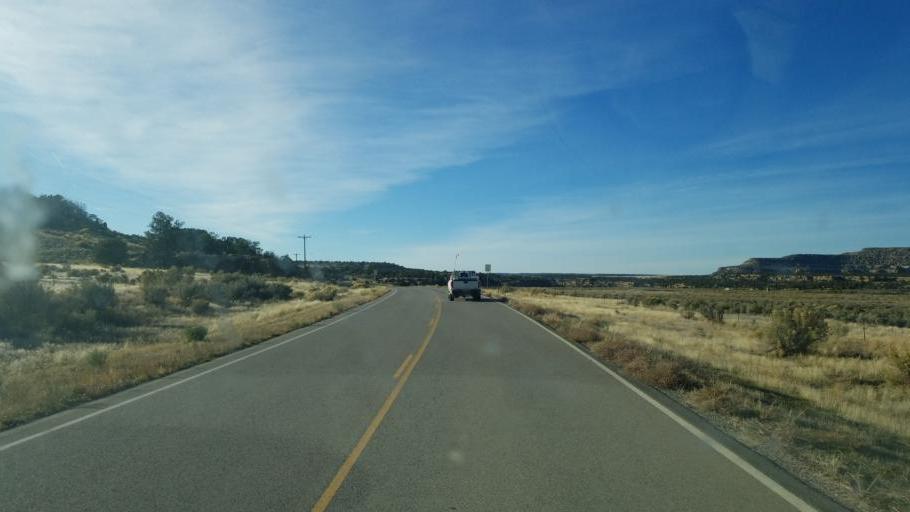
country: US
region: New Mexico
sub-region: San Juan County
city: Bloomfield
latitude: 36.7458
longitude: -107.5832
